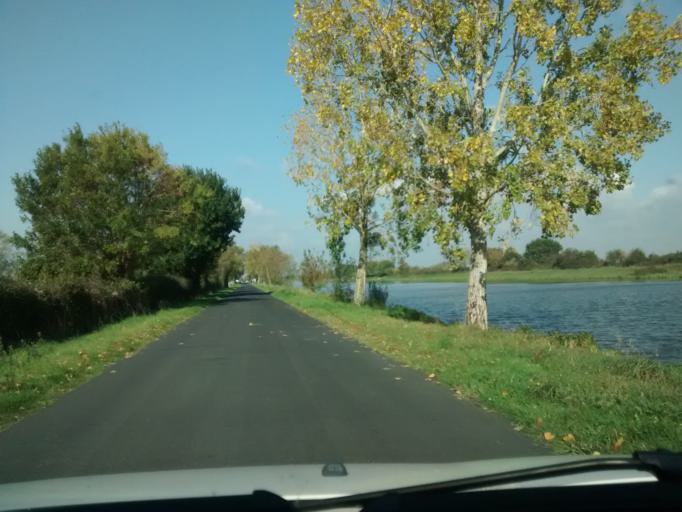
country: FR
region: Pays de la Loire
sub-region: Departement de la Loire-Atlantique
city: Frossay
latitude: 47.2533
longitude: -1.9050
